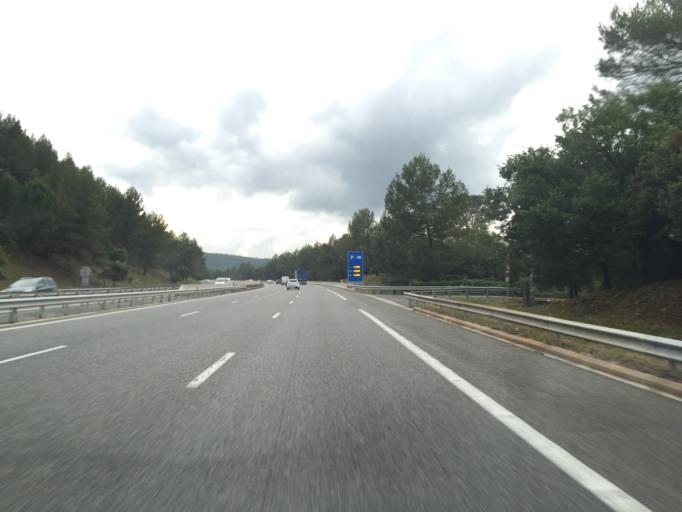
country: FR
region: Provence-Alpes-Cote d'Azur
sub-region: Departement du Var
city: Cabasse
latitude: 43.4032
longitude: 6.2143
